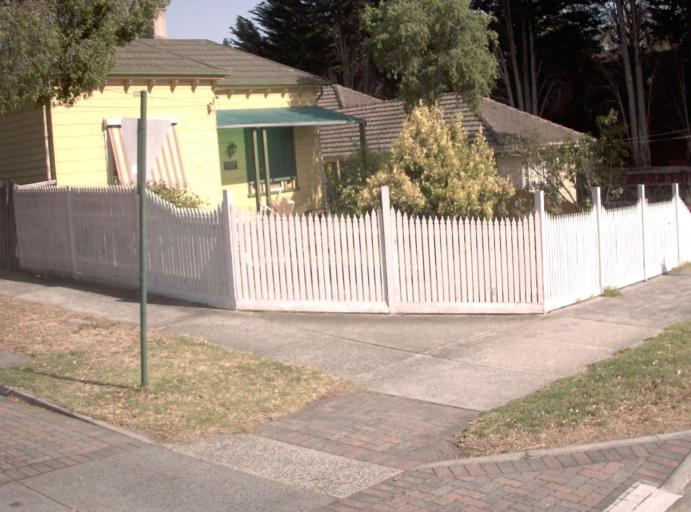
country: AU
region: Victoria
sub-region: Whitehorse
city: Box Hill
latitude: -37.8237
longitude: 145.1227
